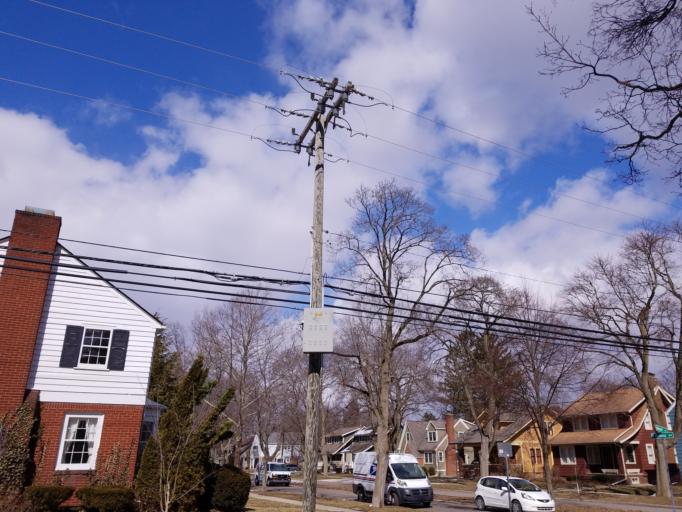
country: US
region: Michigan
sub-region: Washtenaw County
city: Ann Arbor
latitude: 42.2800
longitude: -83.7657
